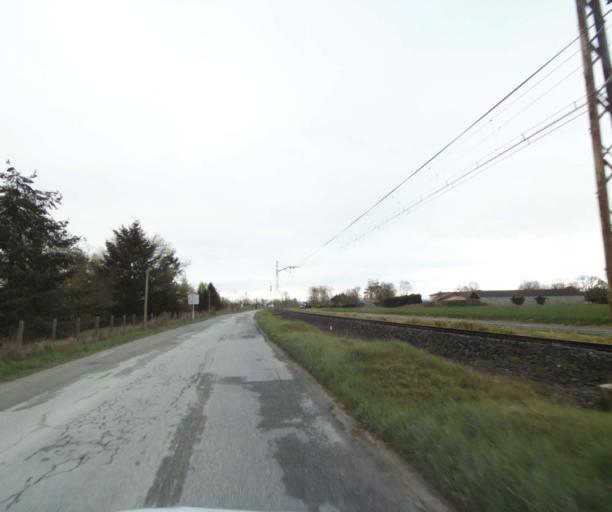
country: FR
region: Midi-Pyrenees
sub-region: Departement de l'Ariege
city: Saverdun
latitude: 43.2274
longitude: 1.6087
